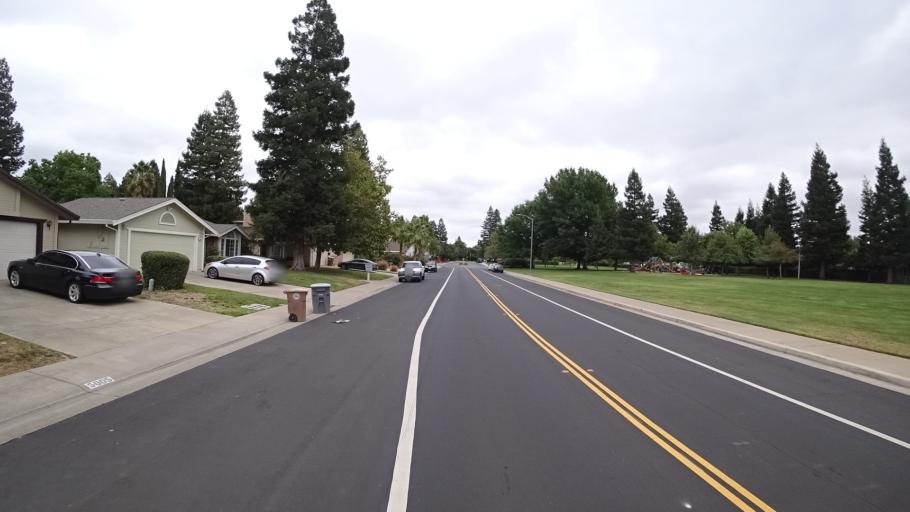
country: US
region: California
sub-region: Sacramento County
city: Laguna
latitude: 38.4205
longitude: -121.4396
